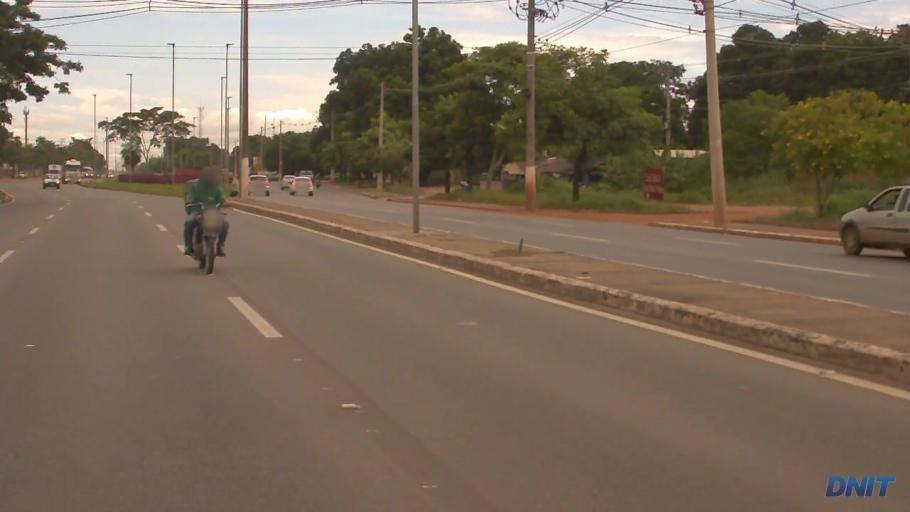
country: BR
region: Mato Grosso
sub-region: Cuiaba
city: Cuiaba
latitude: -15.6444
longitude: -56.0131
